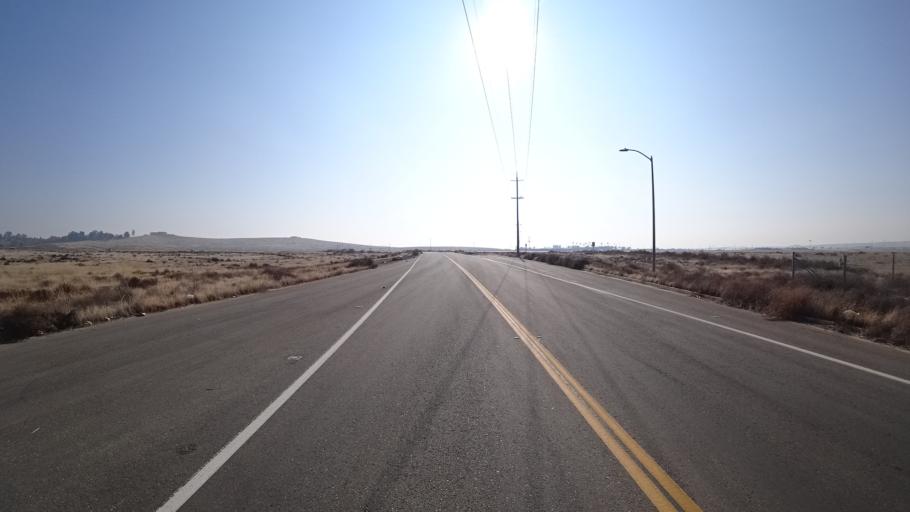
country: US
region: California
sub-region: Kern County
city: Oildale
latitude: 35.4033
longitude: -118.8787
